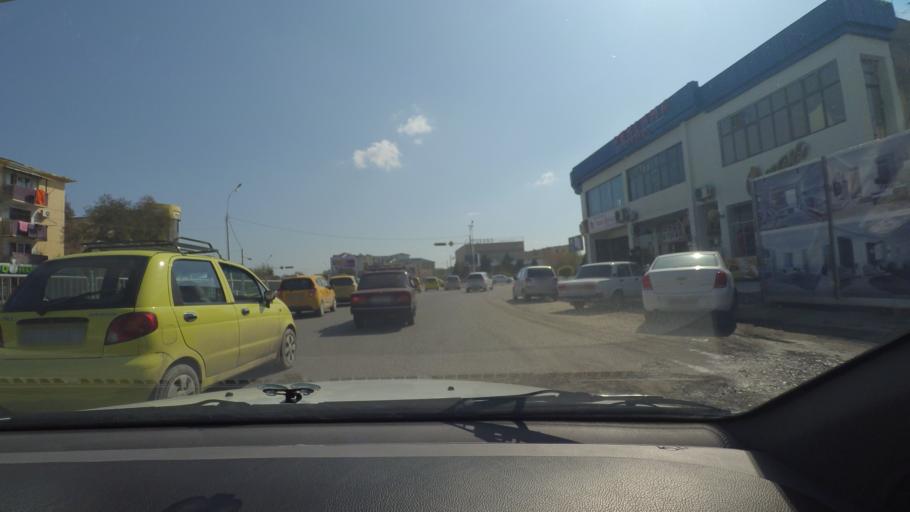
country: UZ
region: Bukhara
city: Bukhara
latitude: 39.7632
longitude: 64.4305
